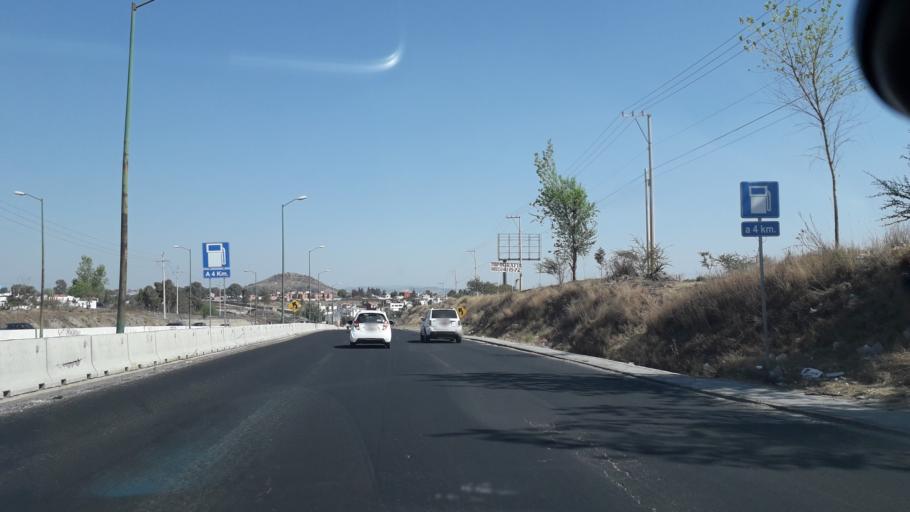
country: MX
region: Puebla
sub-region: Puebla
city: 18 de Marzo
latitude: 18.9753
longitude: -98.2115
